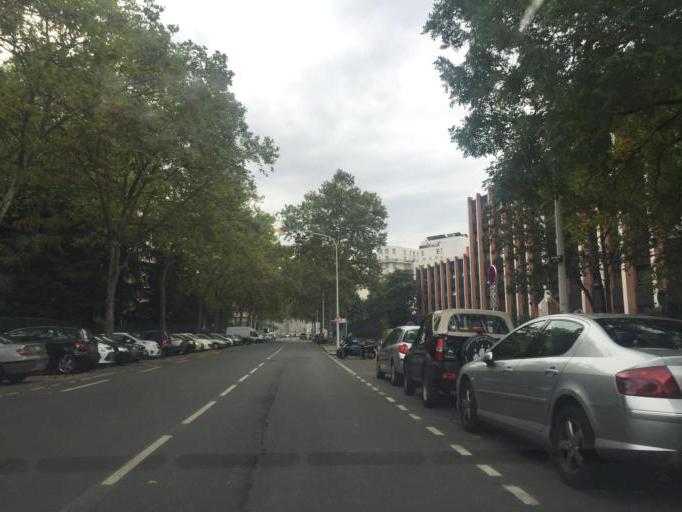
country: FR
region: Rhone-Alpes
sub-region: Departement du Rhone
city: Lyon
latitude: 45.7435
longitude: 4.8594
